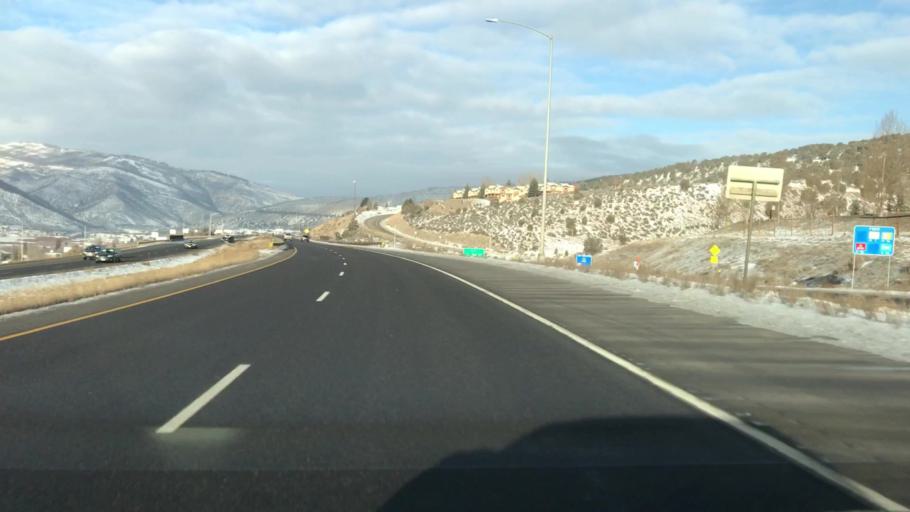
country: US
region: Colorado
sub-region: Eagle County
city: Edwards
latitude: 39.6487
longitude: -106.5848
